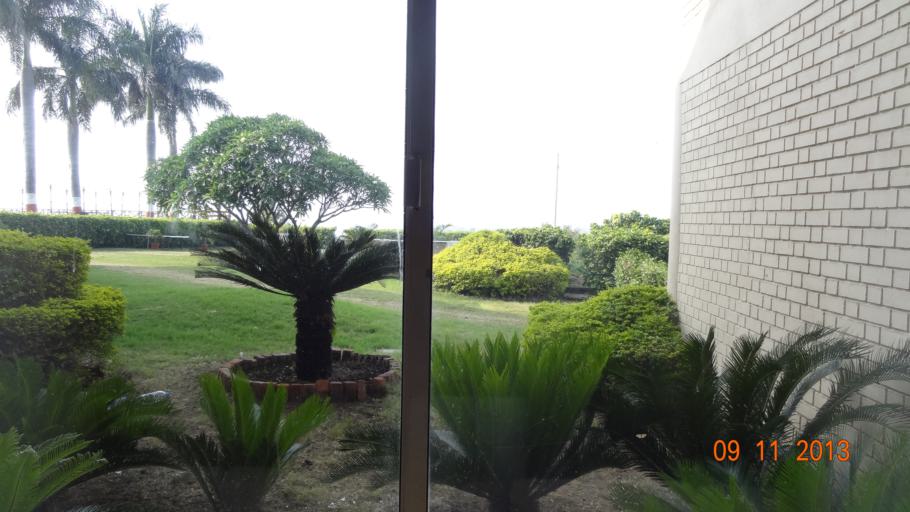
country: IN
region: Madhya Pradesh
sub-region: Indore
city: Indore
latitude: 22.6184
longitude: 75.8058
